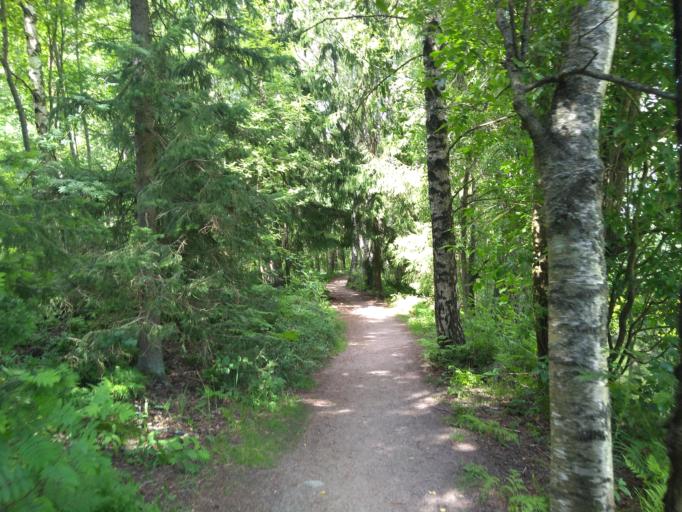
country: FI
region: Uusimaa
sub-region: Helsinki
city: Vantaa
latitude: 60.2163
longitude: 25.0120
